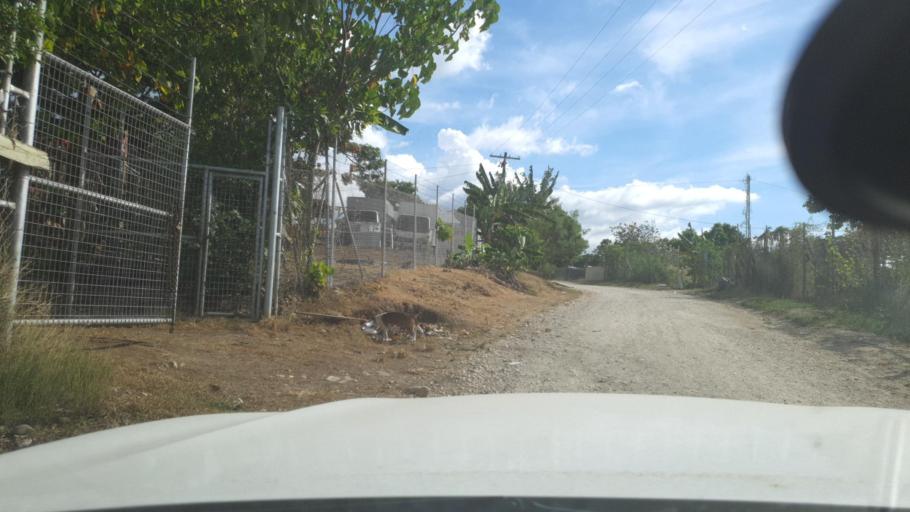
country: SB
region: Guadalcanal
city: Honiara
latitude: -9.4367
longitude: 159.9471
